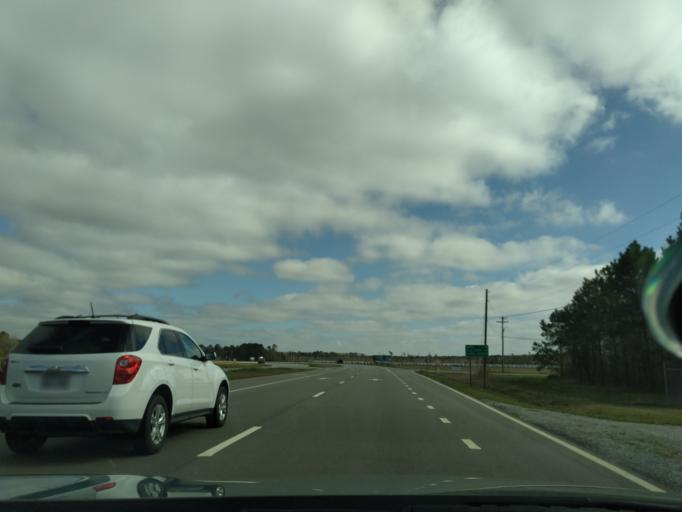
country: US
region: North Carolina
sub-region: Perquimans County
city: Hertford
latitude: 36.1319
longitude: -76.4945
